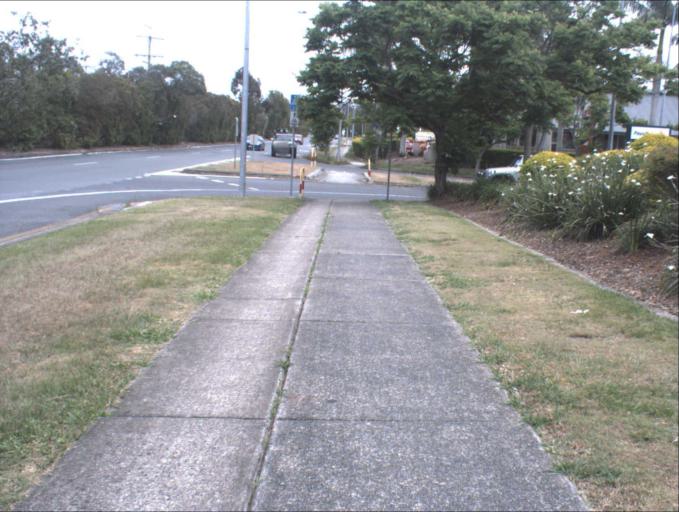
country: AU
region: Queensland
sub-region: Logan
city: Slacks Creek
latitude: -27.6597
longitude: 153.1688
